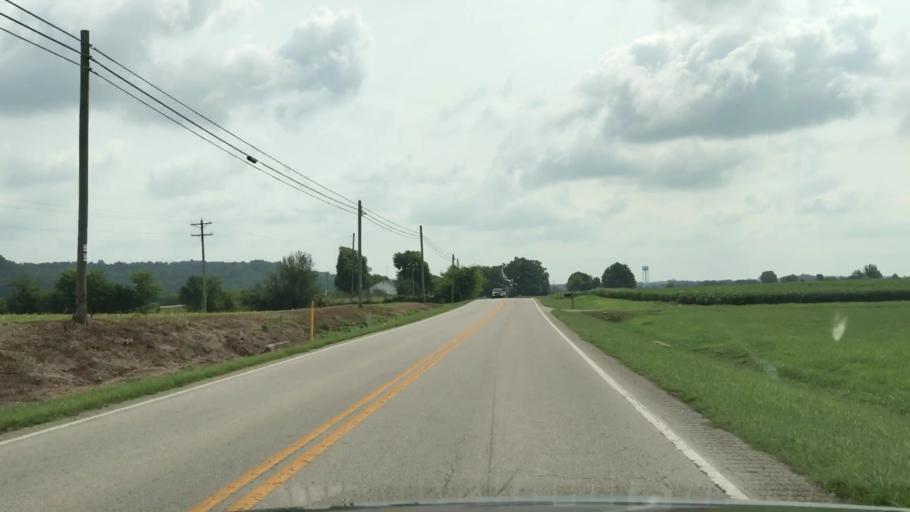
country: US
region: Kentucky
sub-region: Barren County
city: Cave City
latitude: 37.0924
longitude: -86.0986
